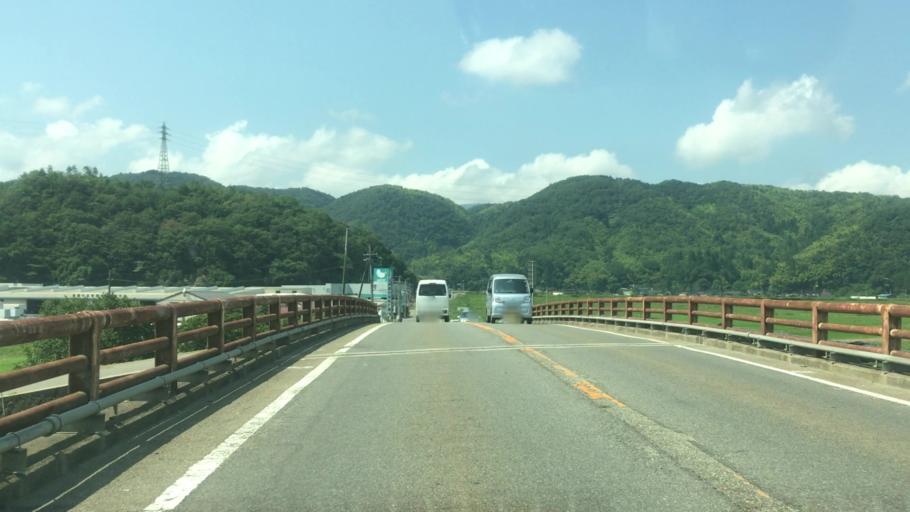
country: JP
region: Hyogo
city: Toyooka
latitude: 35.5587
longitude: 134.7967
